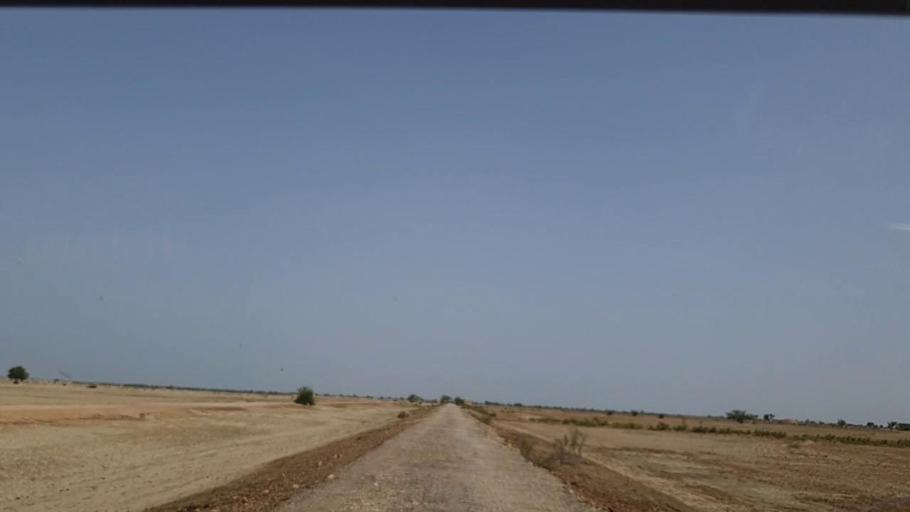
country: PK
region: Sindh
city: Johi
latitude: 26.7689
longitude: 67.6580
